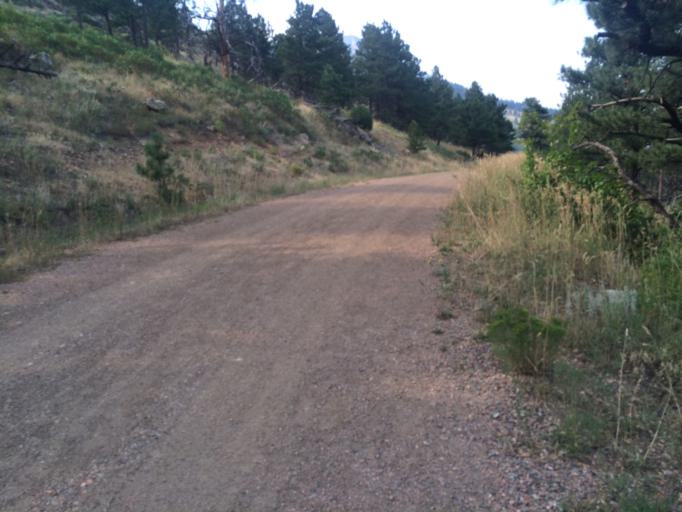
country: US
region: Colorado
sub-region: Boulder County
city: Boulder
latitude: 39.9289
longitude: -105.2739
